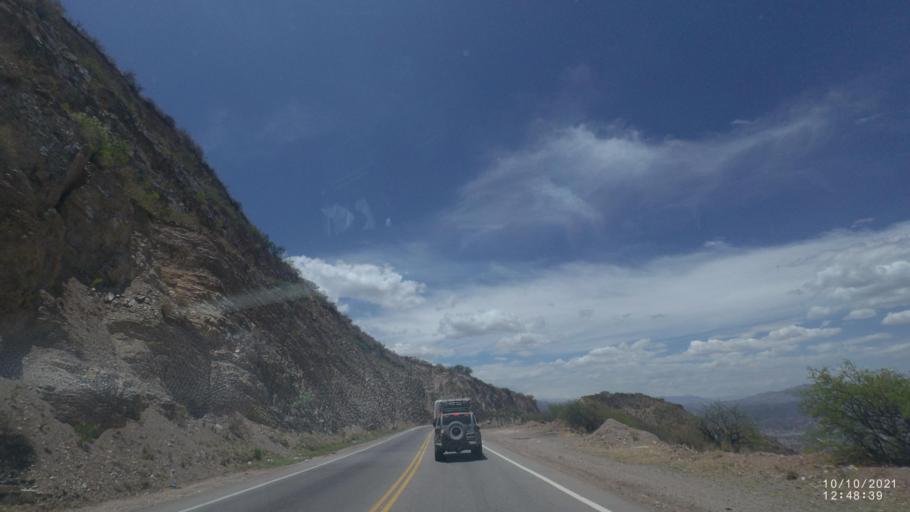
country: BO
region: Cochabamba
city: Irpa Irpa
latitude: -17.6249
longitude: -66.3595
